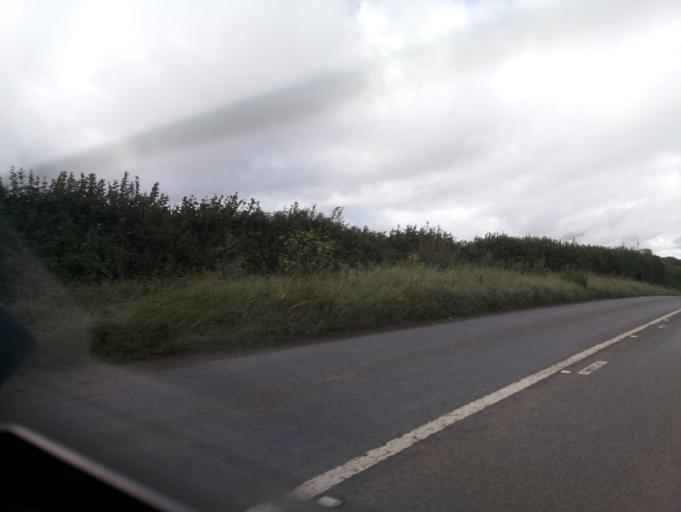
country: GB
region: England
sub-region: Devon
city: Kingsbridge
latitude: 50.3063
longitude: -3.7837
